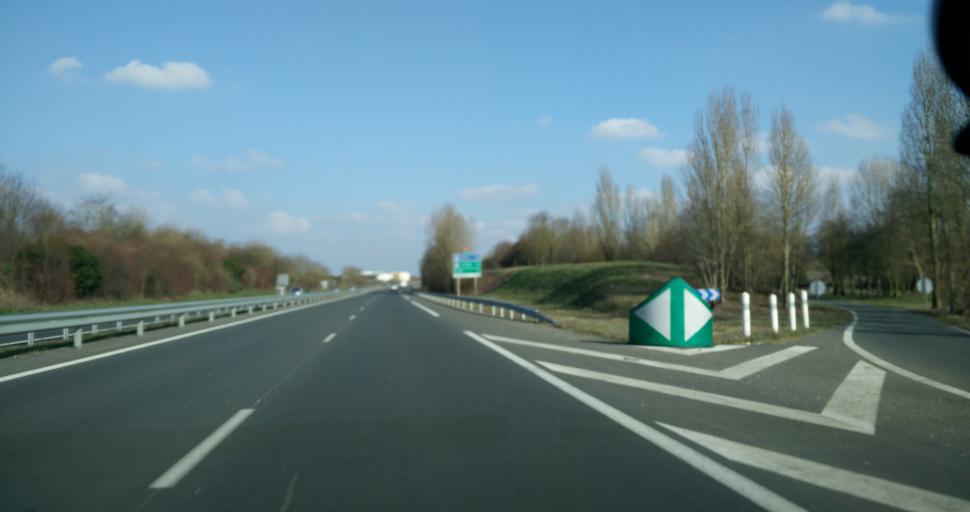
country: FR
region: Poitou-Charentes
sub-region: Departement de la Charente-Maritime
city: Sainte-Soulle
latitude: 46.2041
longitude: -1.0207
